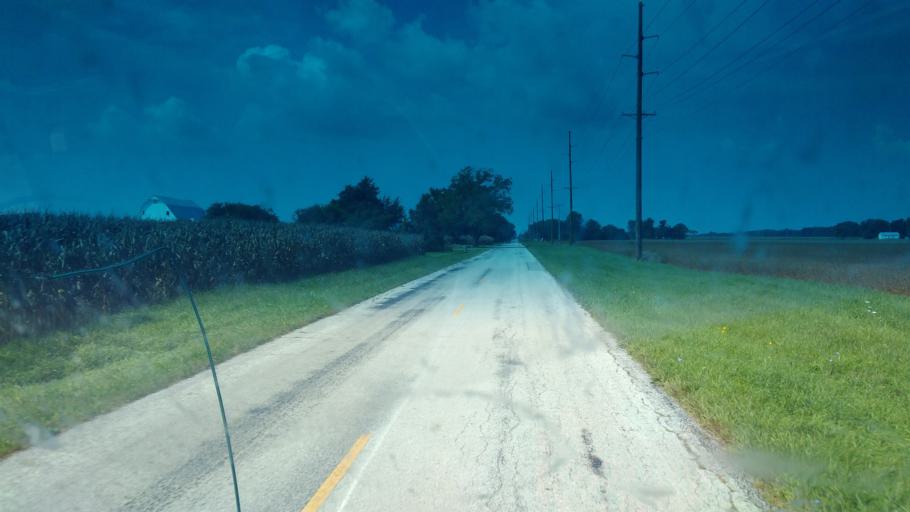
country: US
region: Ohio
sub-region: Union County
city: Richwood
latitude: 40.6002
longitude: -83.3343
